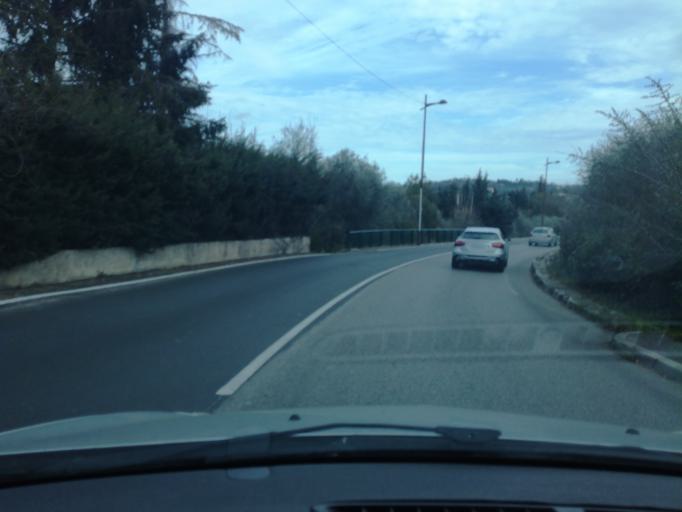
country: FR
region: Provence-Alpes-Cote d'Azur
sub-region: Departement des Alpes-Maritimes
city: Grasse
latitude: 43.6553
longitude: 6.9415
